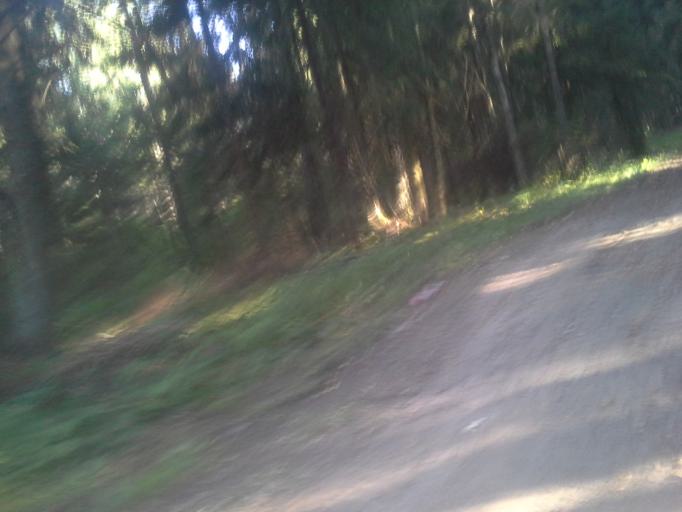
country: RU
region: Moskovskaya
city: Selyatino
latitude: 55.4640
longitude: 36.9892
